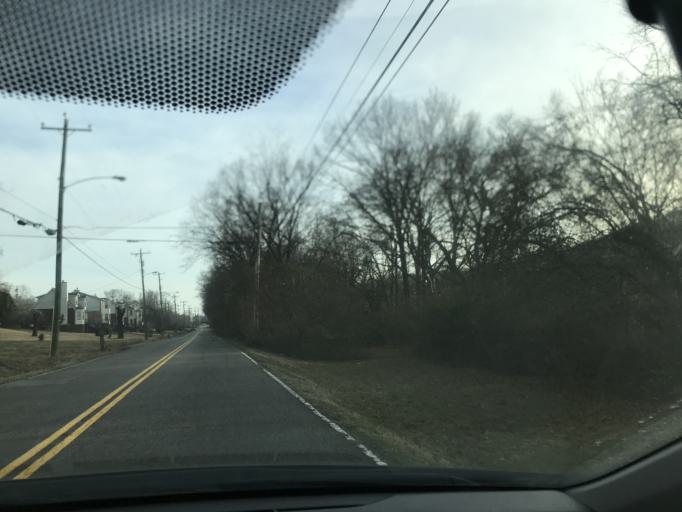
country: US
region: Tennessee
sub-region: Davidson County
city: Nashville
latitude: 36.2082
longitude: -86.8230
